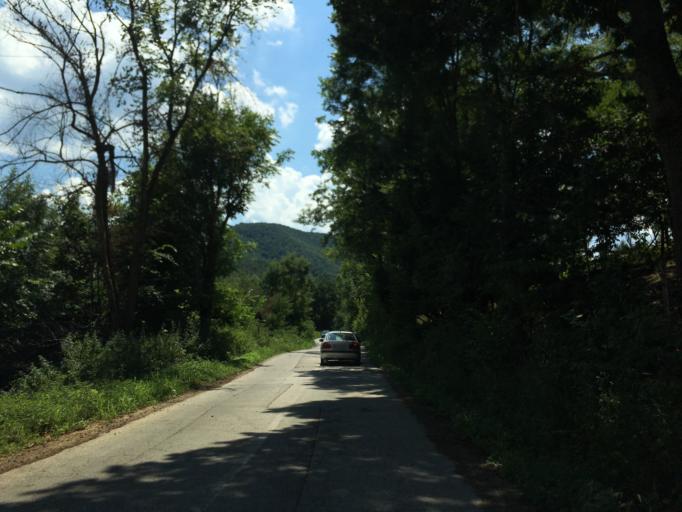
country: RS
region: Central Serbia
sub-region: Kolubarski Okrug
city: Ljig
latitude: 44.2346
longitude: 20.3523
